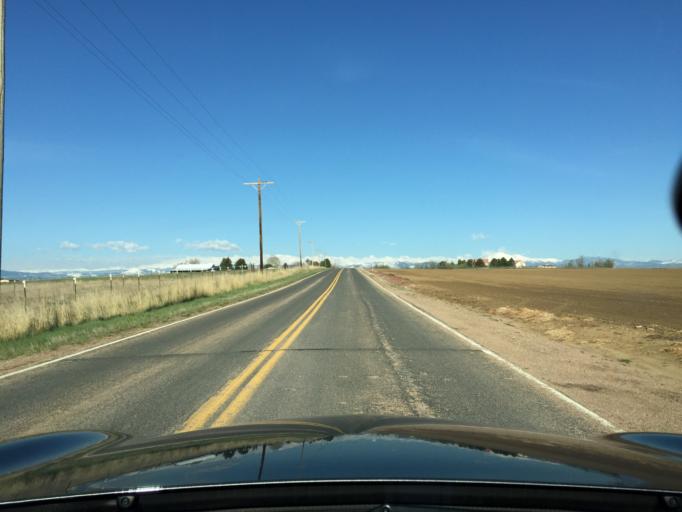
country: US
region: Colorado
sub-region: Boulder County
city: Erie
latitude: 40.1020
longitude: -105.0558
